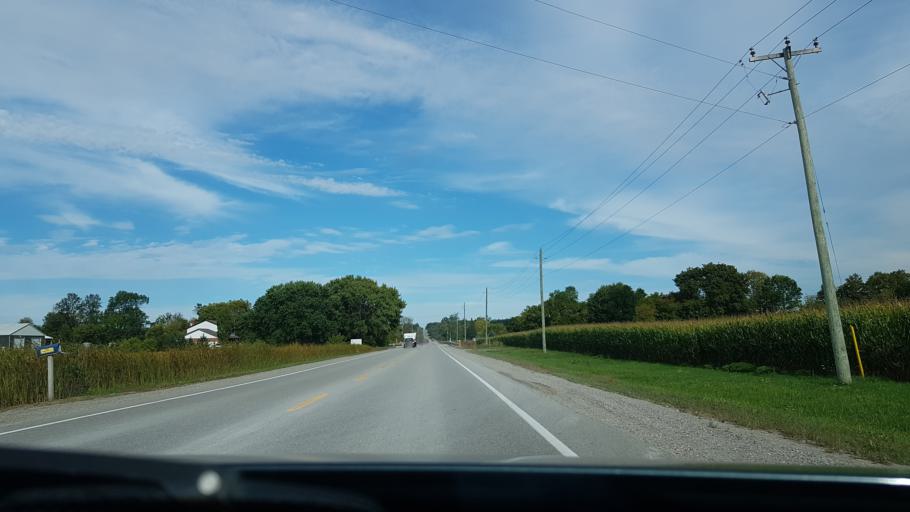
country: CA
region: Ontario
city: Angus
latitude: 44.4747
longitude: -79.8466
